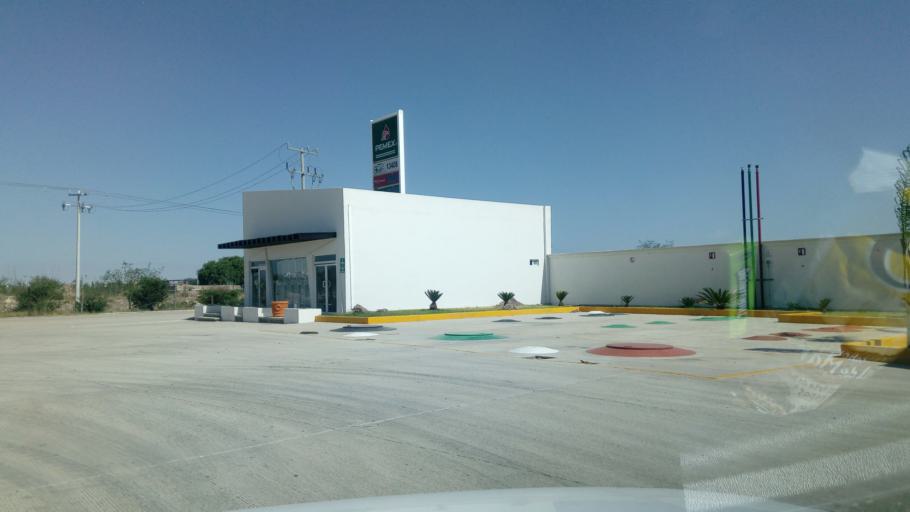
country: MX
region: Durango
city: Victoria de Durango
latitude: 23.9871
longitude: -104.6894
